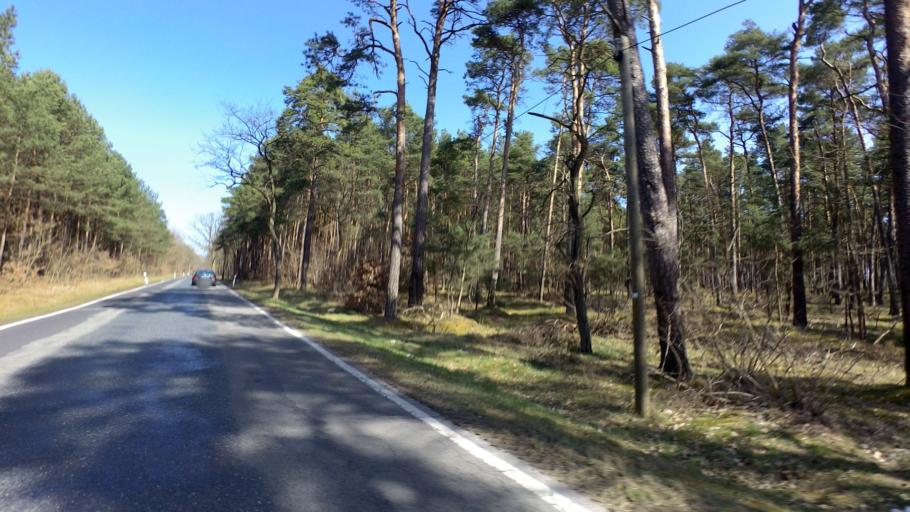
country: DE
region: Brandenburg
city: Ruthnick
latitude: 52.9135
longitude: 12.9582
